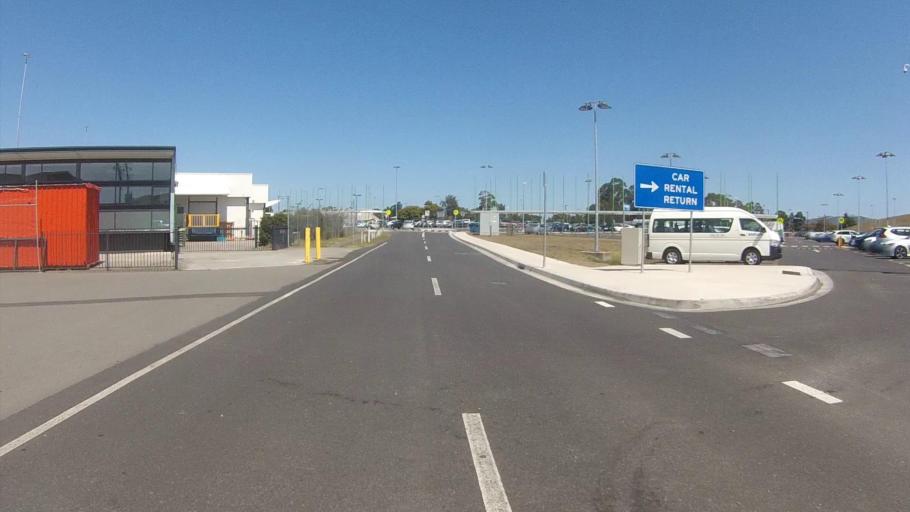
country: AU
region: Tasmania
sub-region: Clarence
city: Seven Mile Beach
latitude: -42.8358
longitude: 147.5035
